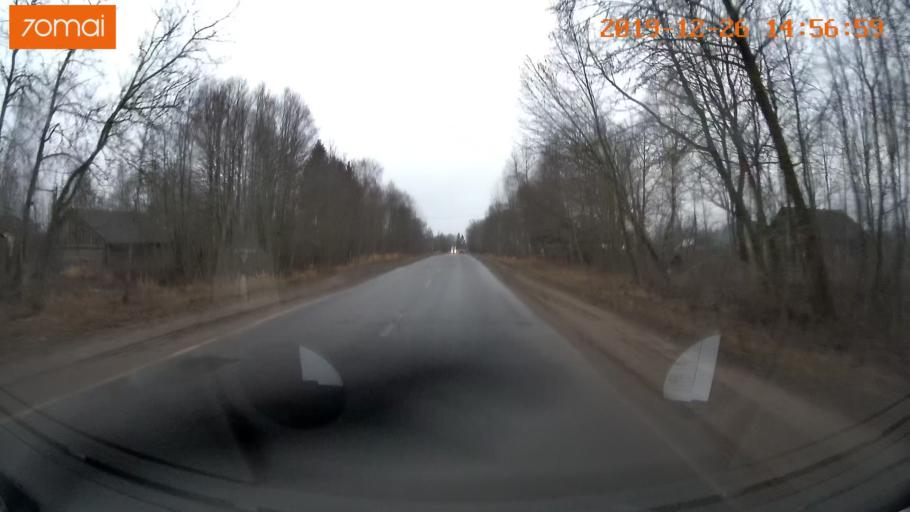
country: RU
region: Jaroslavl
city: Rybinsk
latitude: 58.2872
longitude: 38.8669
